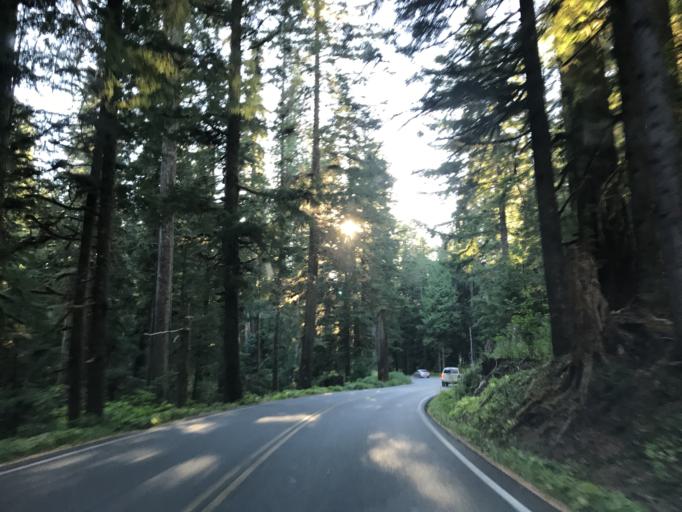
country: US
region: Washington
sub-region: Pierce County
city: Eatonville
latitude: 46.7349
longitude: -121.8421
